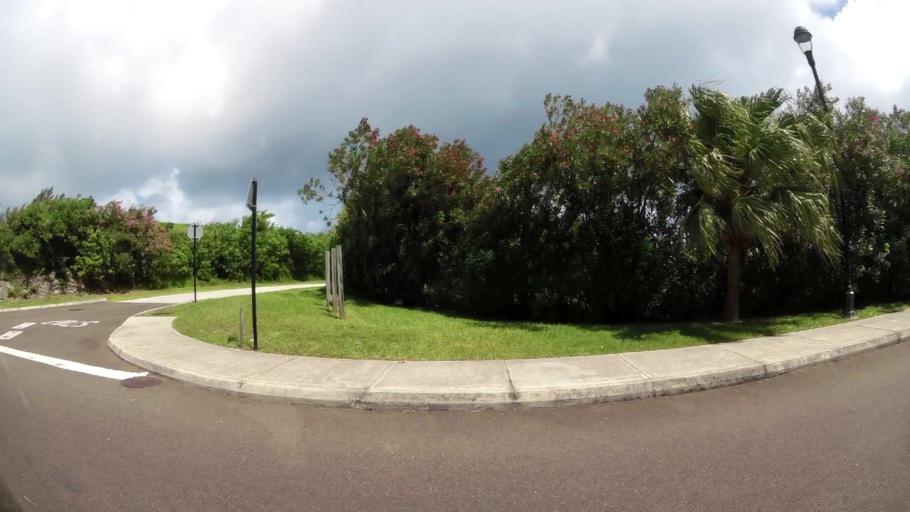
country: BM
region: Saint George
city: Saint George
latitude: 32.3641
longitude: -64.6637
